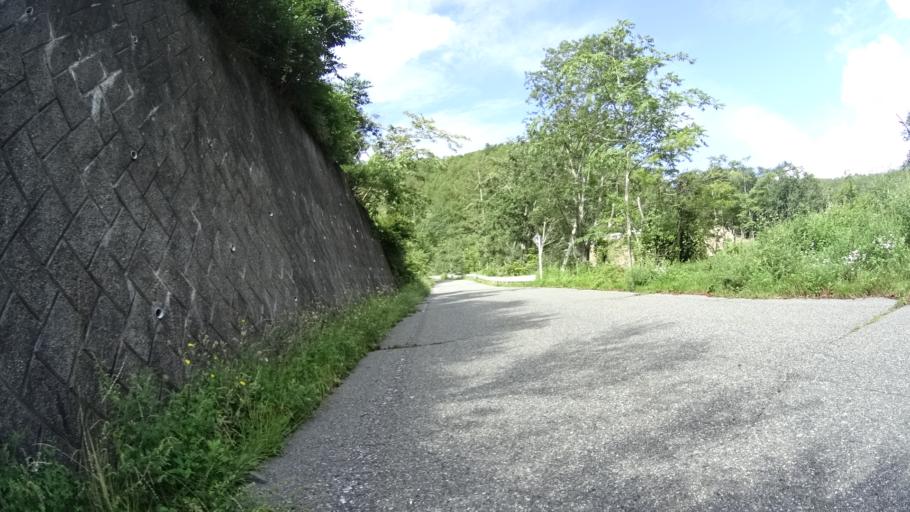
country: JP
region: Yamanashi
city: Nirasaki
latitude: 35.9111
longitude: 138.5404
